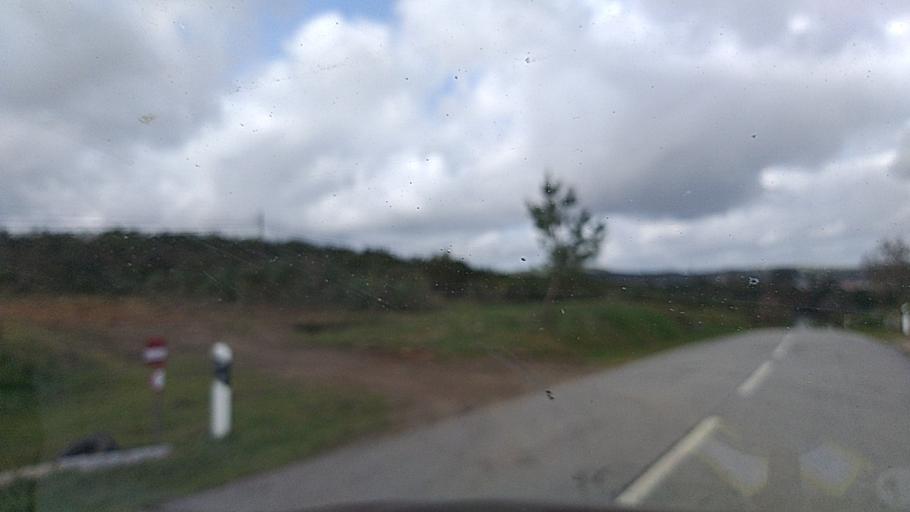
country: PT
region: Guarda
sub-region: Fornos de Algodres
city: Fornos de Algodres
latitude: 40.6544
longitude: -7.5511
